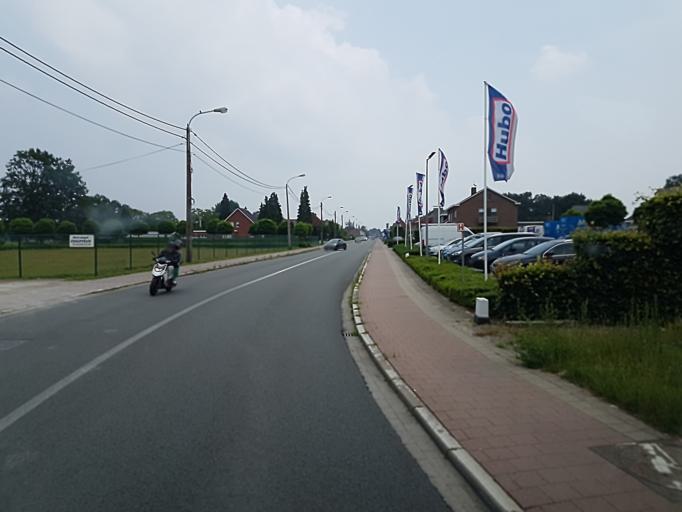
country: BE
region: Flanders
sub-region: Provincie Antwerpen
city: Nijlen
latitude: 51.1682
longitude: 4.6535
